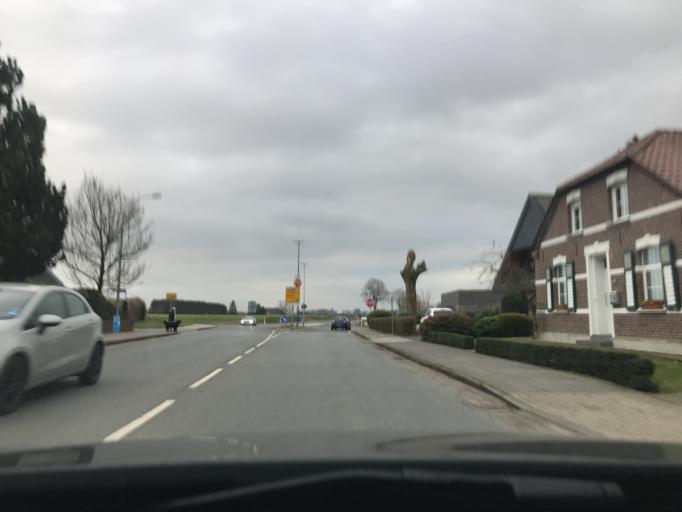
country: DE
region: North Rhine-Westphalia
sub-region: Regierungsbezirk Dusseldorf
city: Uedem
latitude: 51.6613
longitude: 6.2760
